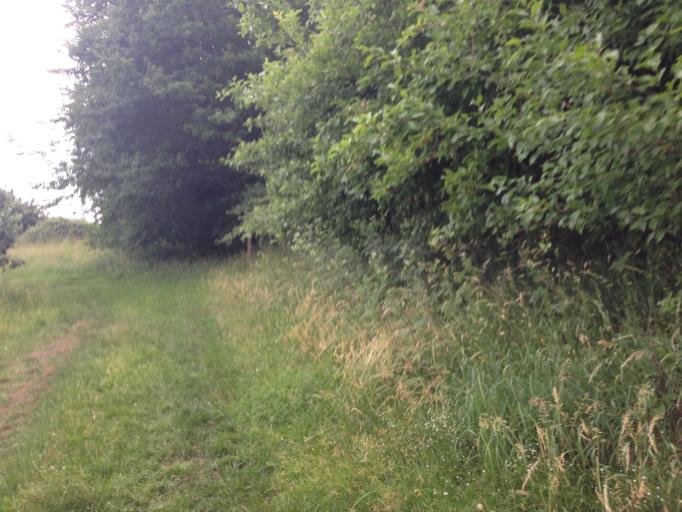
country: DE
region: Hesse
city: Wetter
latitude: 50.8547
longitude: 8.7284
